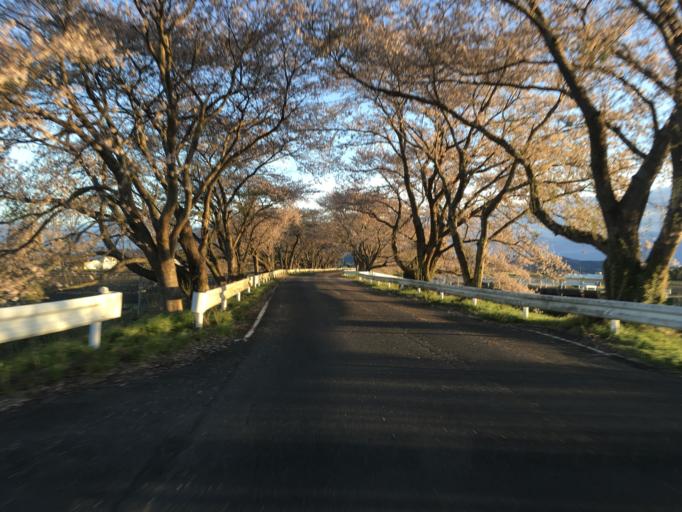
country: JP
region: Miyagi
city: Wakuya
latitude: 38.6556
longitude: 141.1465
